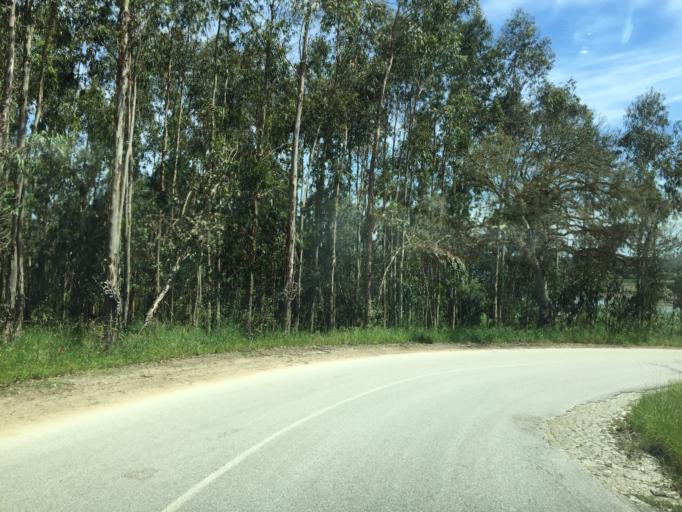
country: PT
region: Leiria
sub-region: Pombal
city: Lourical
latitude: 40.0681
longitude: -8.7595
